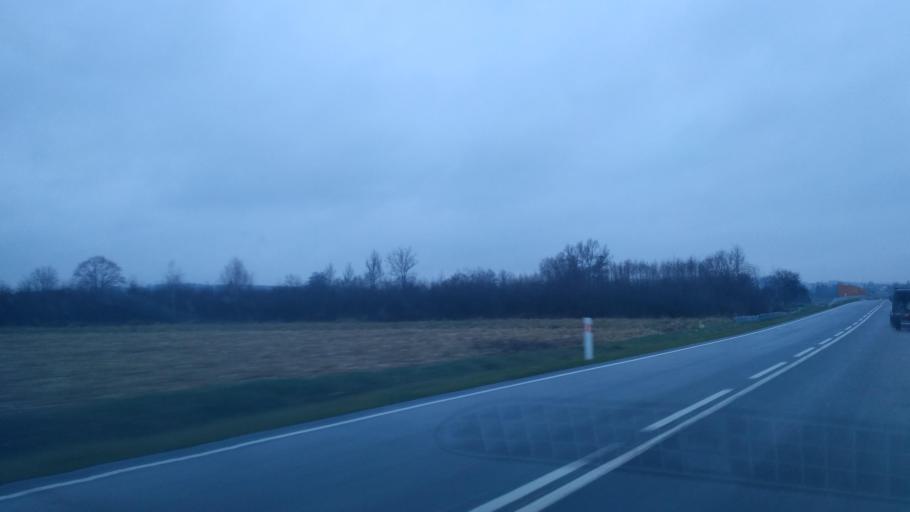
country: PL
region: Subcarpathian Voivodeship
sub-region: Powiat rzeszowski
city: Dynow
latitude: 49.8255
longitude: 22.2416
